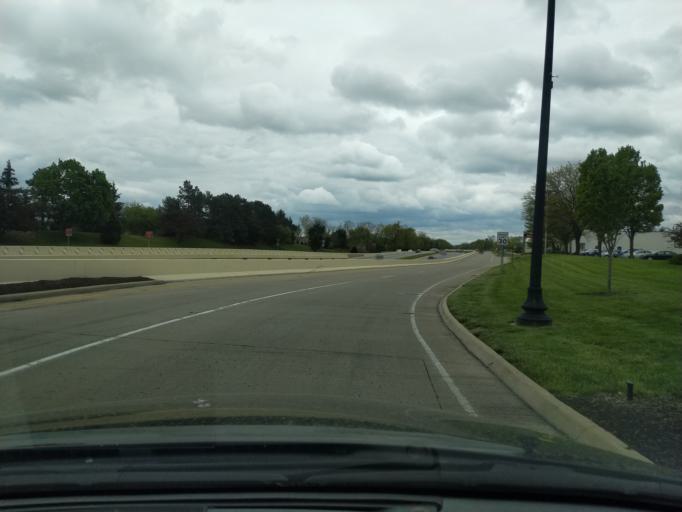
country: US
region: Indiana
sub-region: Hamilton County
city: Carmel
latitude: 39.9616
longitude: -86.1139
